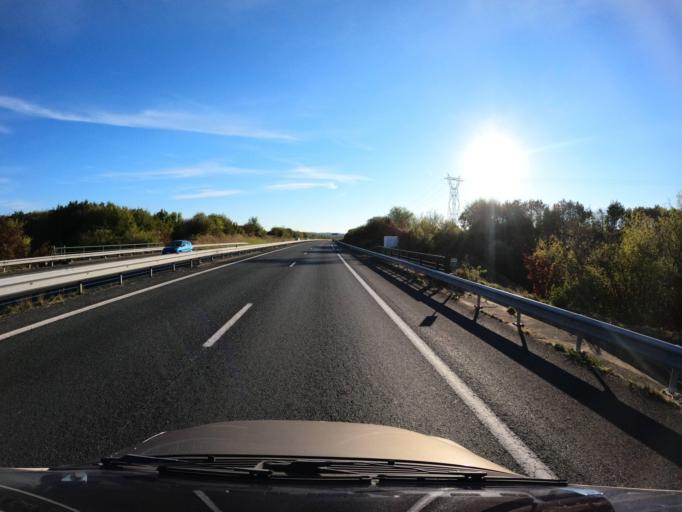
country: FR
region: Pays de la Loire
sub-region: Departement de Maine-et-Loire
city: Mazieres-en-Mauges
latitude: 47.0430
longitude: -0.8414
